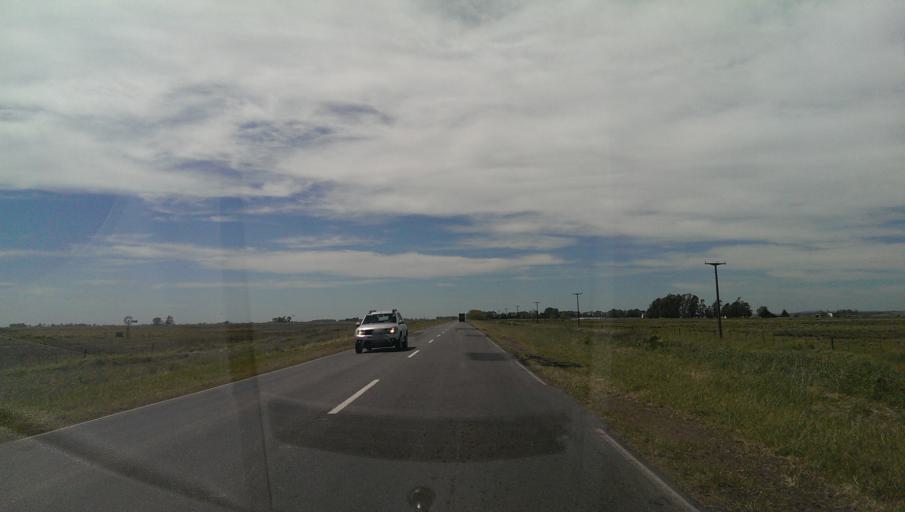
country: AR
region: Buenos Aires
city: Olavarria
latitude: -37.0329
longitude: -60.4268
